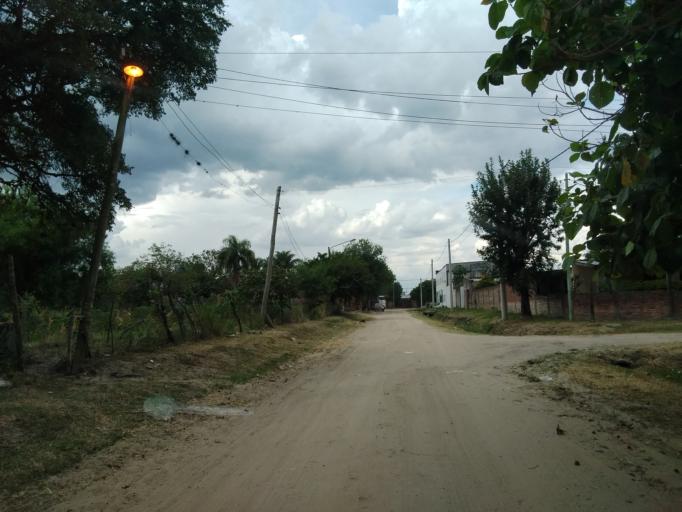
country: AR
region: Corrientes
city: Corrientes
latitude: -27.5233
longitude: -58.7960
